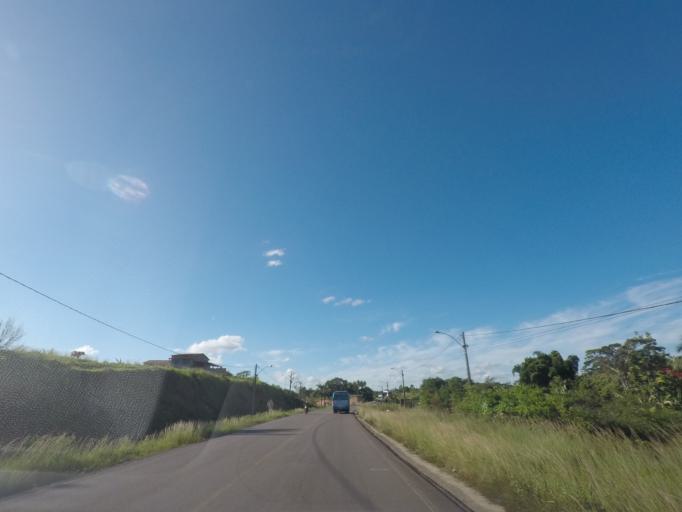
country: BR
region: Bahia
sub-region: Nazare
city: Nazare
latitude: -13.0776
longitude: -38.9985
